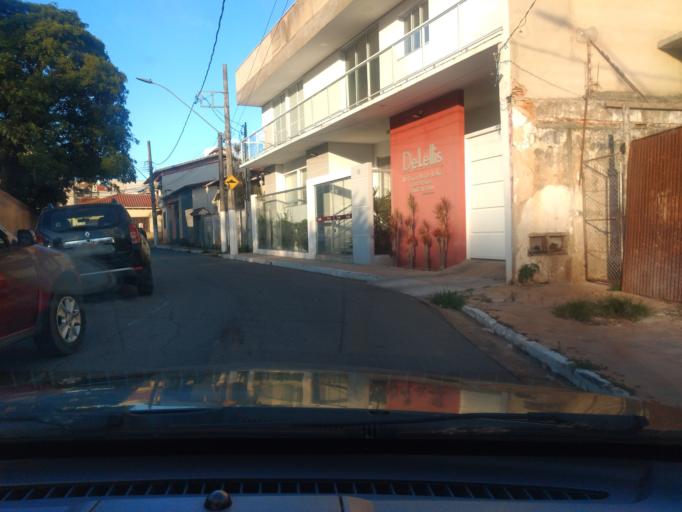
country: BR
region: Minas Gerais
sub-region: Tres Coracoes
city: Tres Coracoes
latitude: -21.6992
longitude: -45.2528
